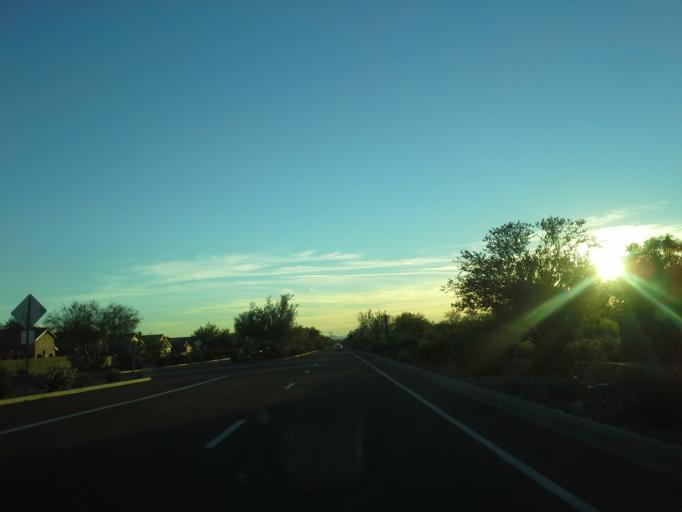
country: US
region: Arizona
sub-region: Pinal County
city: Apache Junction
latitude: 33.3722
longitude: -111.4699
